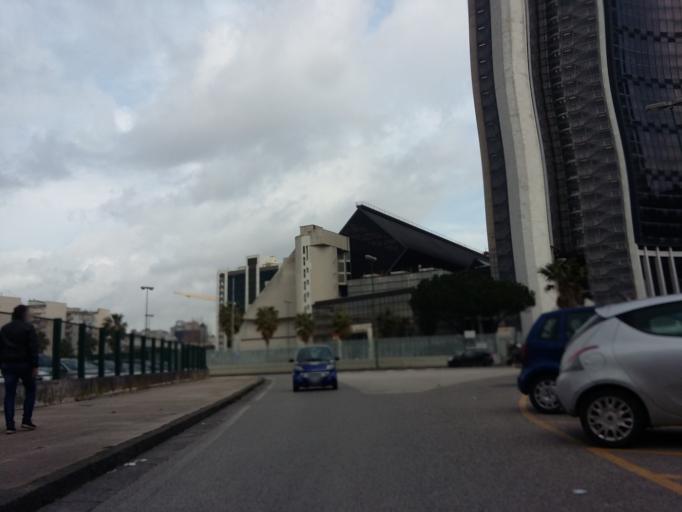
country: IT
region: Campania
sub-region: Provincia di Napoli
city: Napoli
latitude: 40.8595
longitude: 14.2807
